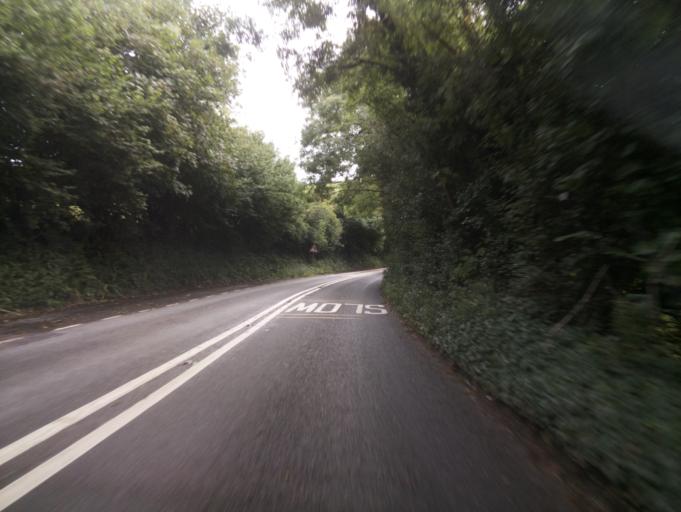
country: GB
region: England
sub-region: Devon
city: Modbury
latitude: 50.3473
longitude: -3.8884
